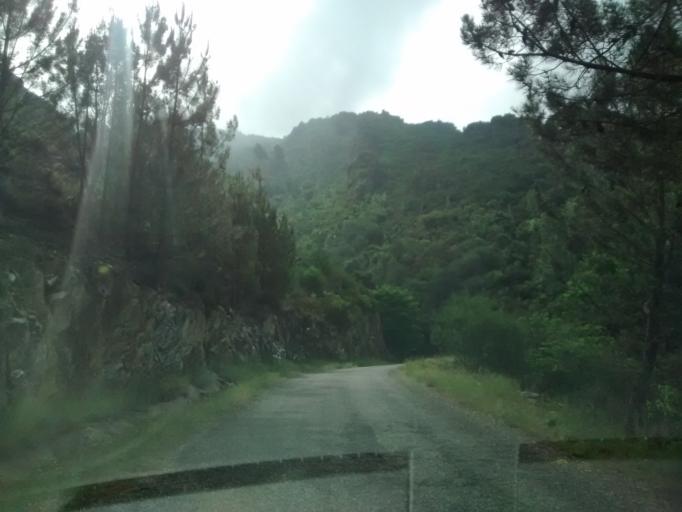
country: ES
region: Galicia
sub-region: Provincia de Ourense
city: Castro Caldelas
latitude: 42.4204
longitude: -7.3865
